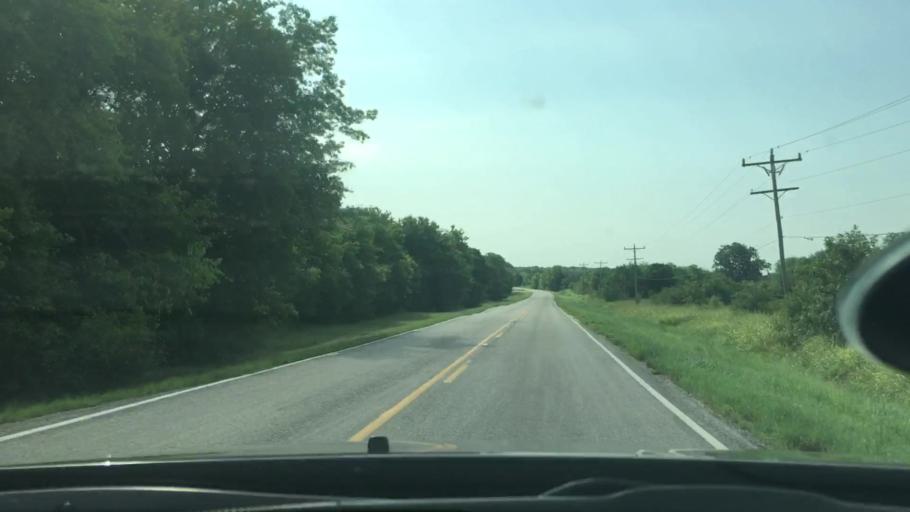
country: US
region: Oklahoma
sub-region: Johnston County
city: Tishomingo
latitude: 34.1470
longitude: -96.5516
